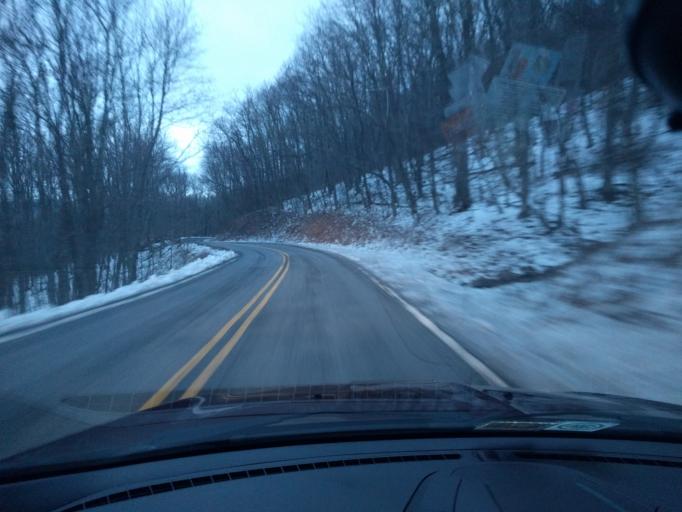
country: US
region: Virginia
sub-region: Alleghany County
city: Clifton Forge
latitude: 37.8847
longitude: -79.8872
